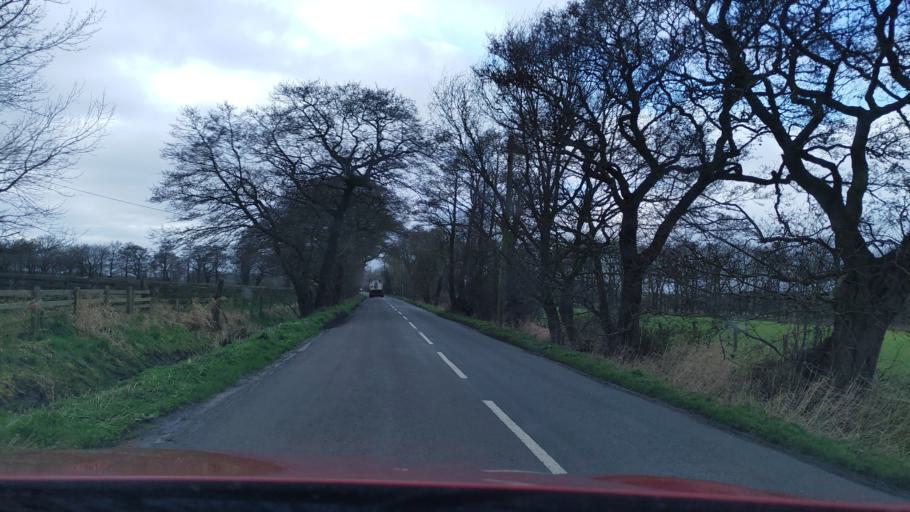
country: GB
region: England
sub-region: Lancashire
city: Tarleton
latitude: 53.6344
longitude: -2.8661
